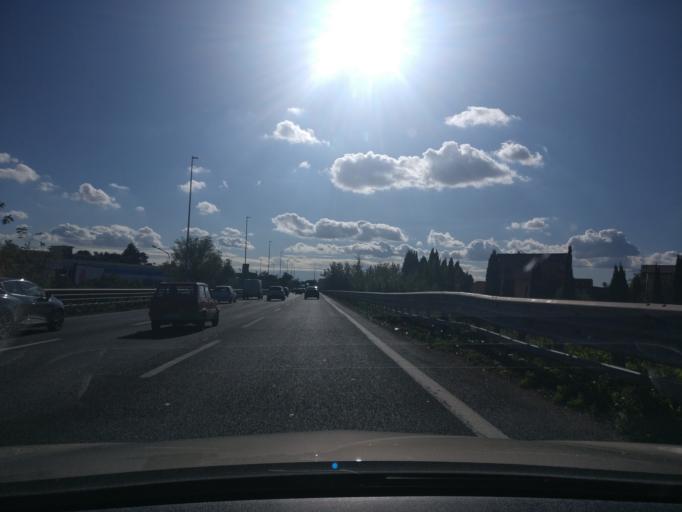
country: IT
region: Latium
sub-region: Citta metropolitana di Roma Capitale
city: Ciampino
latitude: 41.8302
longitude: 12.5830
